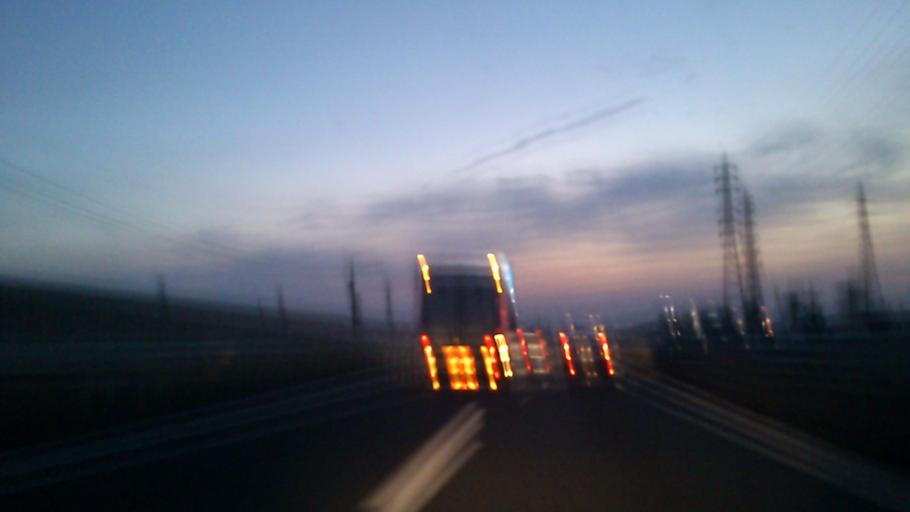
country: JP
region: Aichi
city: Komaki
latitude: 35.2977
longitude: 136.9270
